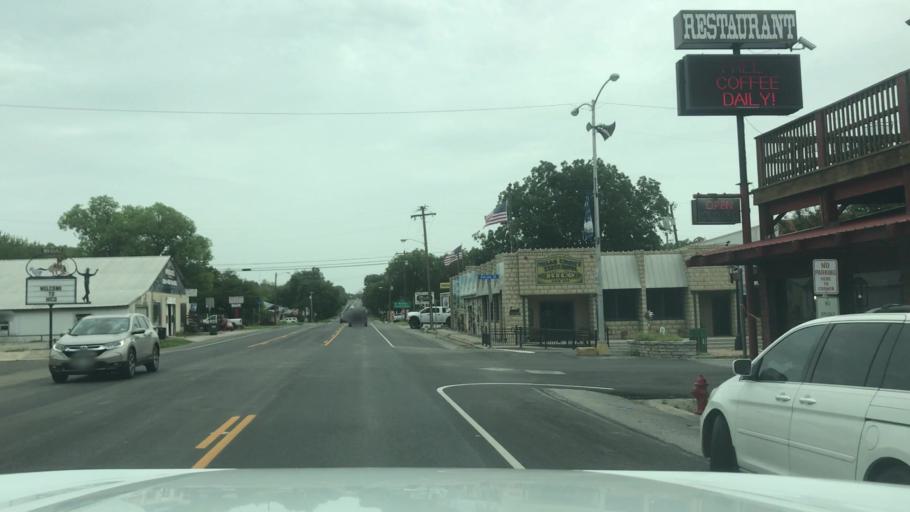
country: US
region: Texas
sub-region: Hamilton County
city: Hico
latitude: 31.9824
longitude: -98.0309
